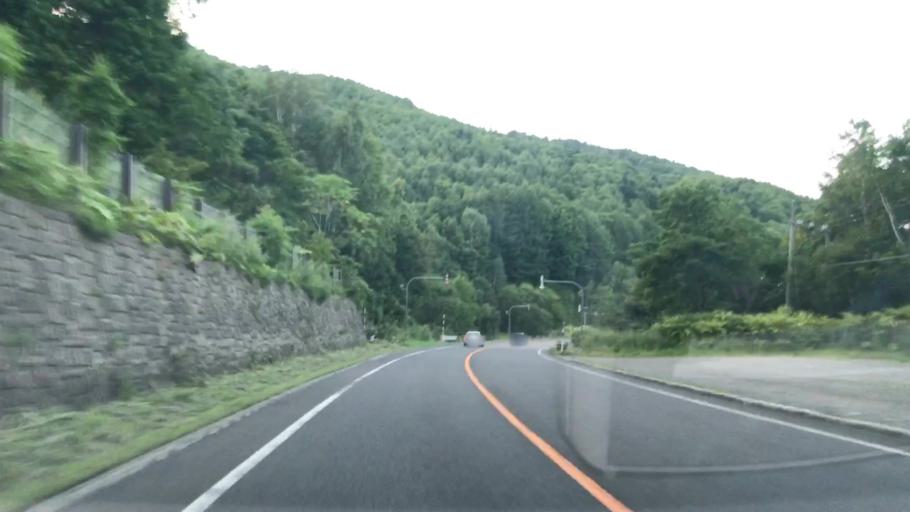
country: JP
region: Hokkaido
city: Sapporo
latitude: 42.9096
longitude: 141.1201
